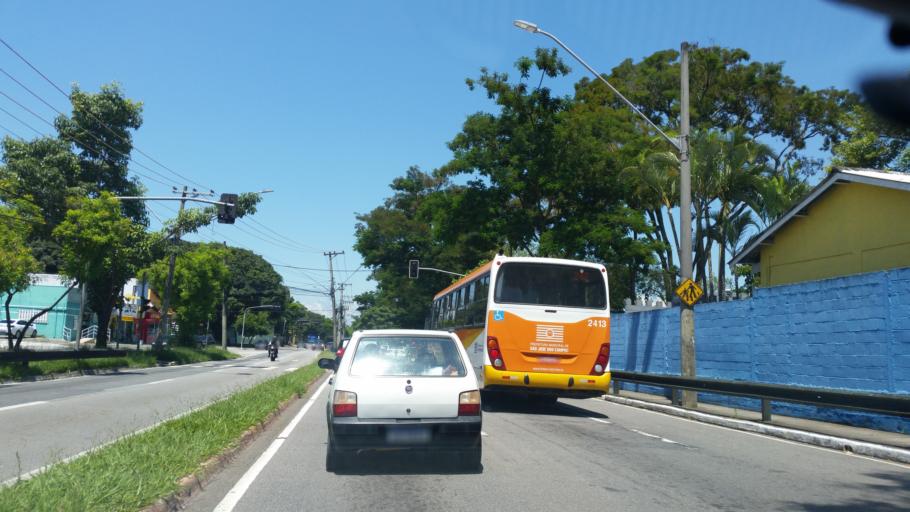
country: BR
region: Sao Paulo
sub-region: Sao Jose Dos Campos
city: Sao Jose dos Campos
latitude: -23.1760
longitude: -45.8256
